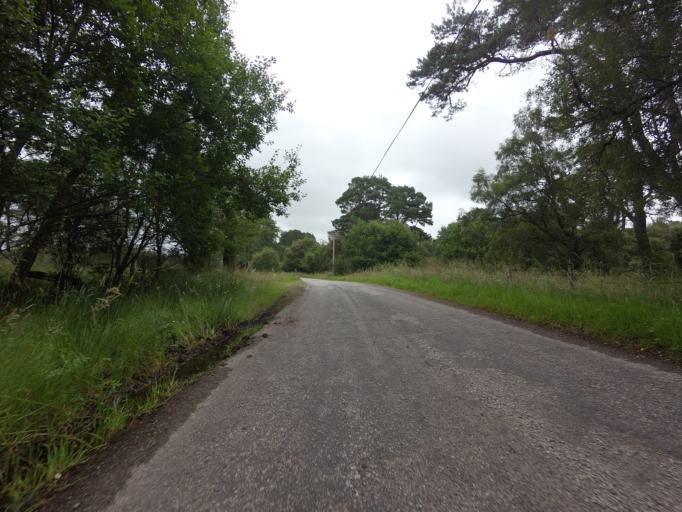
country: GB
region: Scotland
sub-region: Highland
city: Alness
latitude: 57.9881
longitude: -4.4117
